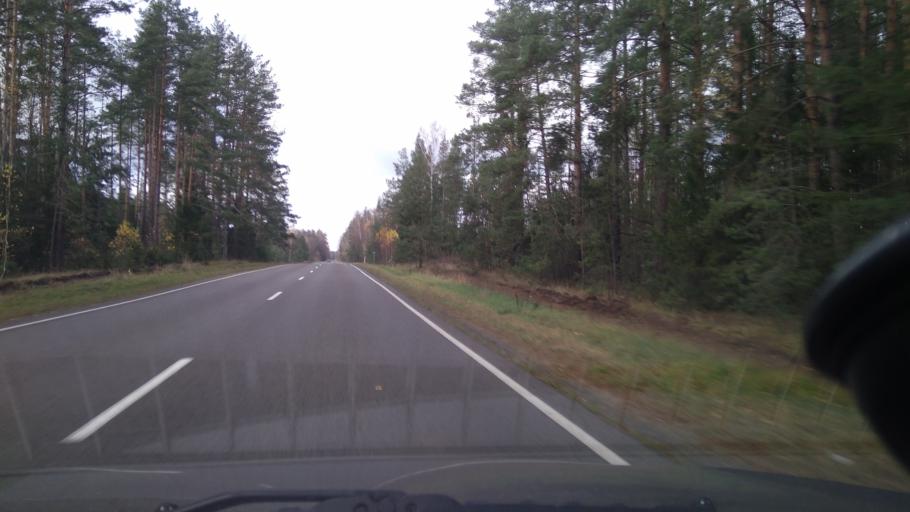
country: BY
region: Minsk
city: Slutsk
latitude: 53.2133
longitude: 27.7570
